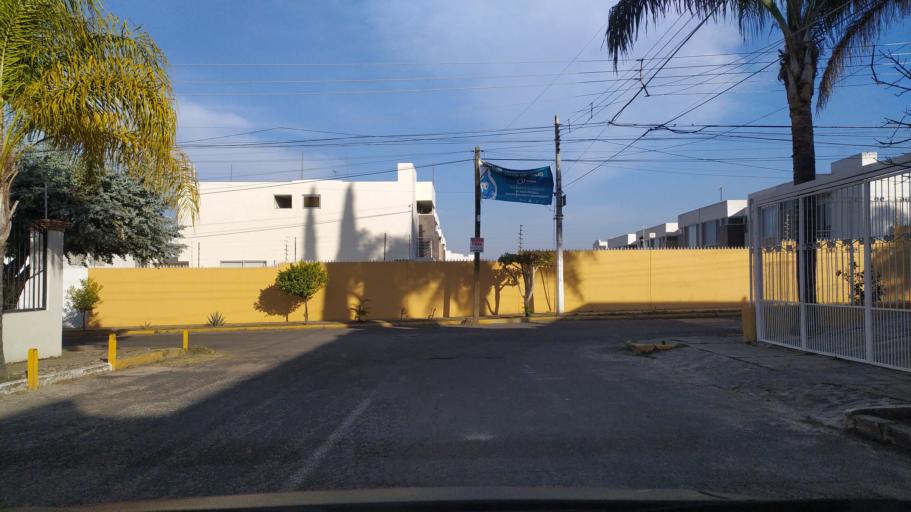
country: MX
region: Jalisco
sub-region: Tlajomulco de Zuniga
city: Palomar
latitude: 20.6265
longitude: -103.4702
